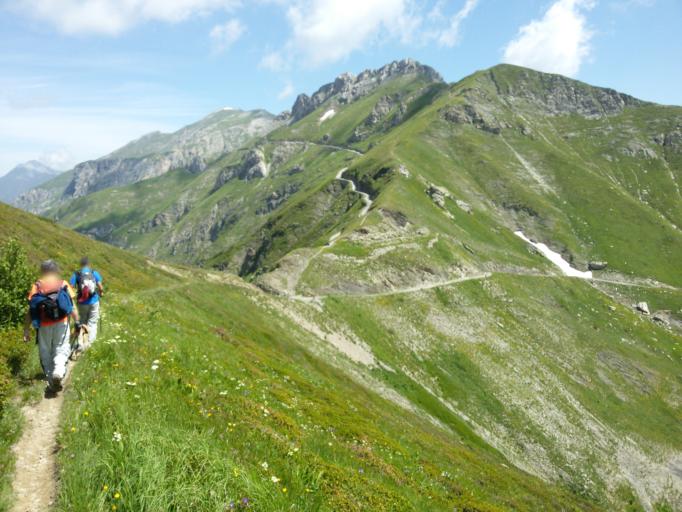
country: IT
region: Piedmont
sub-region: Provincia di Cuneo
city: Limone Piemonte
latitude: 44.1539
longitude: 7.6237
